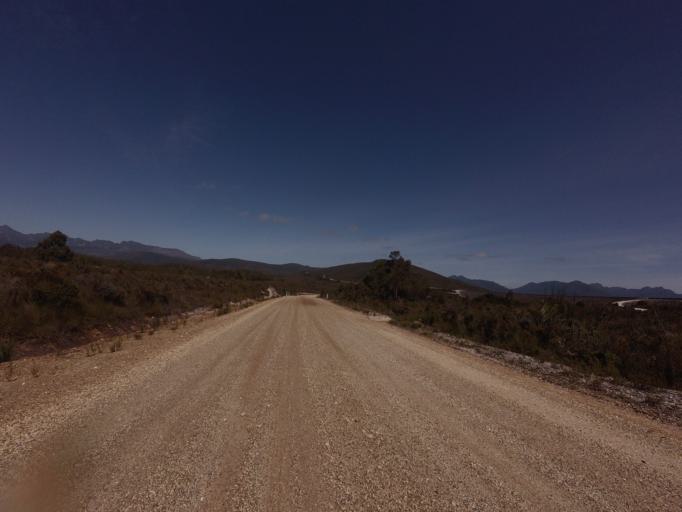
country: AU
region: Tasmania
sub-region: Huon Valley
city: Geeveston
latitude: -43.0317
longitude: 146.3041
